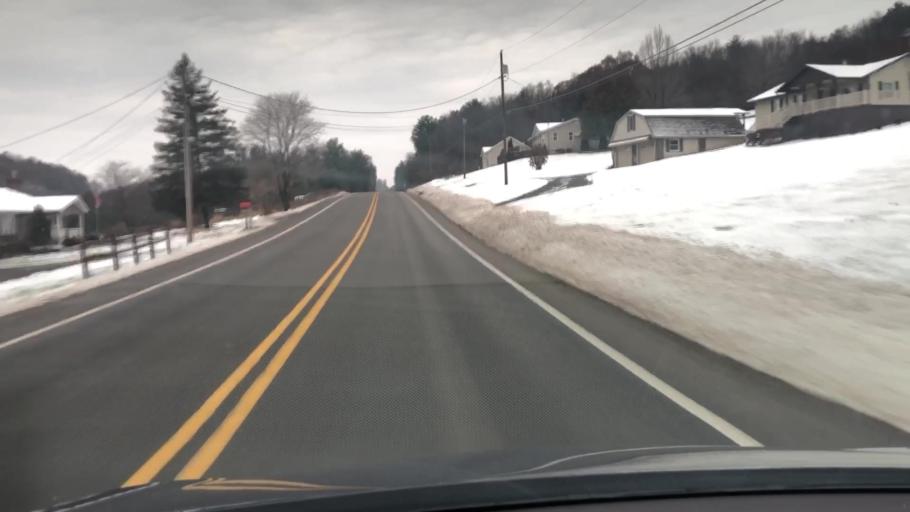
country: US
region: Pennsylvania
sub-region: Jefferson County
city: Brookville
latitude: 41.0440
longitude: -79.2543
